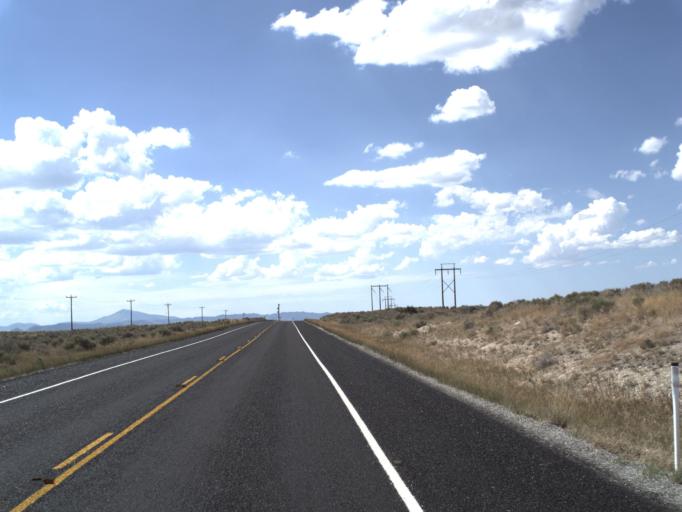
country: US
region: Idaho
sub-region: Minidoka County
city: Rupert
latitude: 41.9878
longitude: -113.1793
